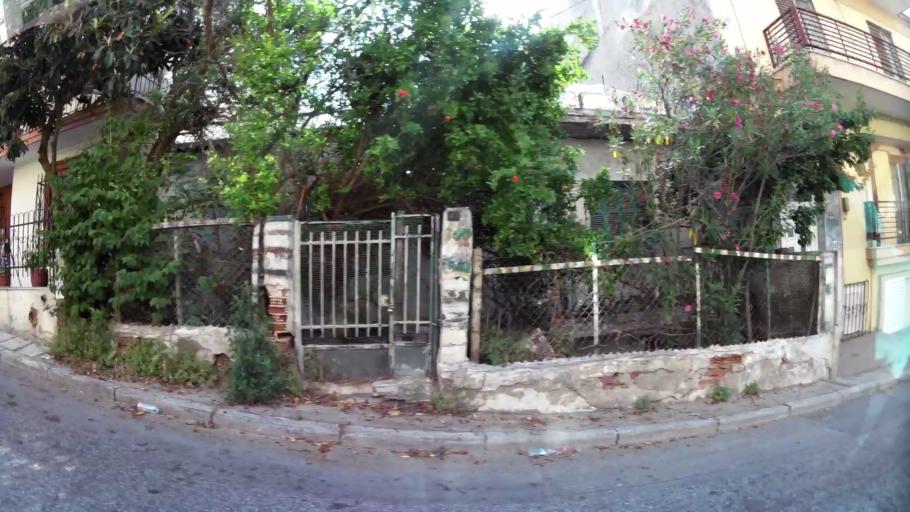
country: GR
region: Central Macedonia
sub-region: Nomos Thessalonikis
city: Sykies
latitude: 40.6462
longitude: 22.9550
